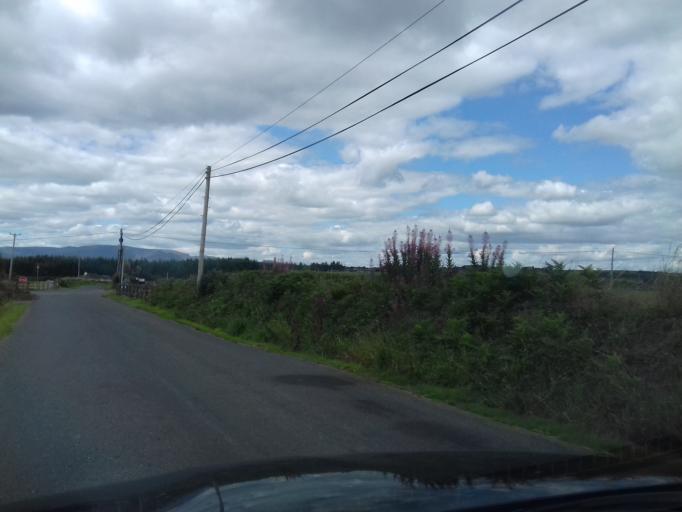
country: IE
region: Munster
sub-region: Waterford
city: Portlaw
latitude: 52.1820
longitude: -7.2989
